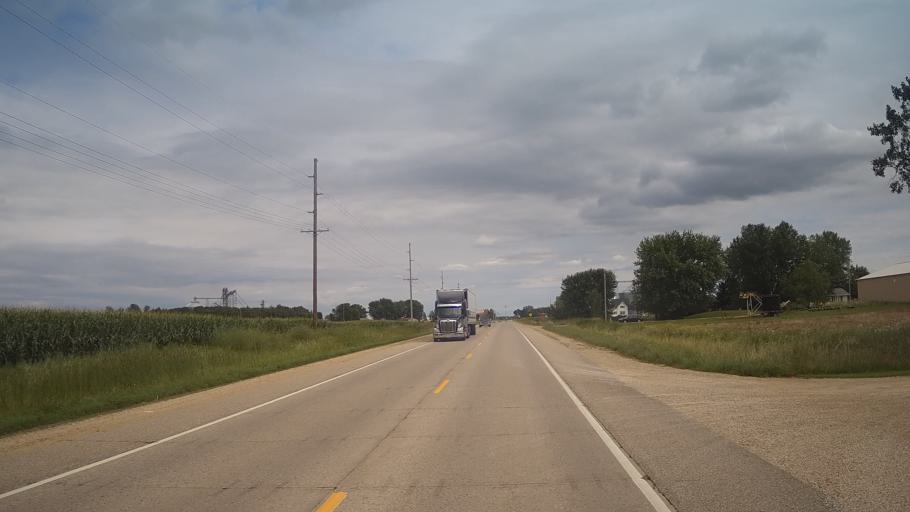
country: US
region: Wisconsin
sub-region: Green Lake County
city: Berlin
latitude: 44.0410
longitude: -88.9948
